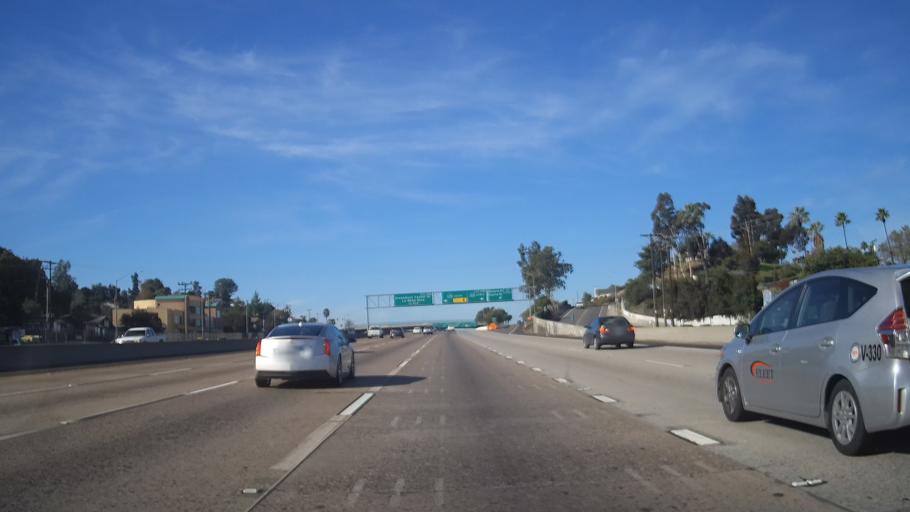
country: US
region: California
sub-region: San Diego County
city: Casa de Oro-Mount Helix
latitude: 32.7788
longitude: -116.9926
